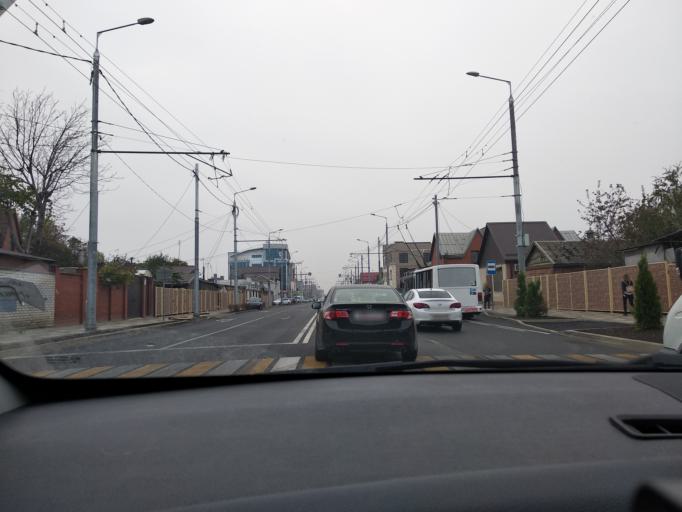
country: RU
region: Krasnodarskiy
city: Krasnodar
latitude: 45.0477
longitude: 38.9580
